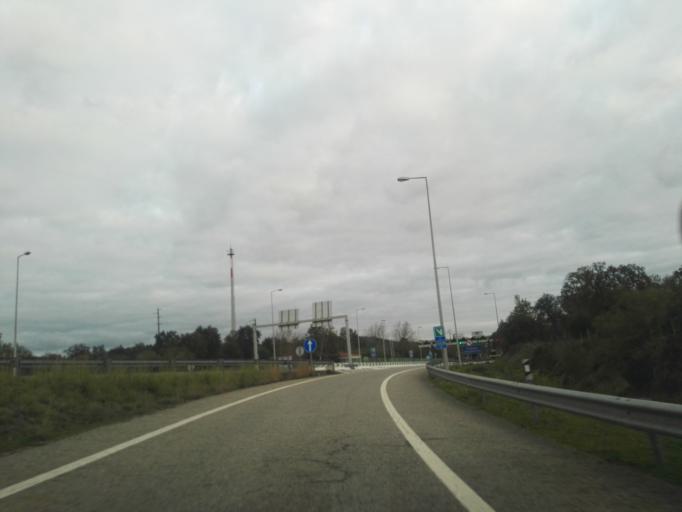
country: PT
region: Evora
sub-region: Montemor-O-Novo
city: Montemor-o-Novo
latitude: 38.6655
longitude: -8.2324
